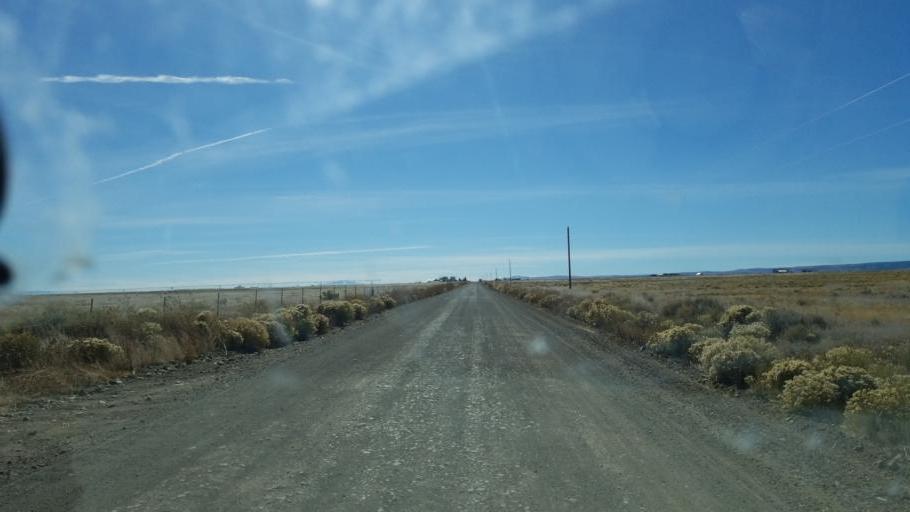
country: US
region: Colorado
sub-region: Rio Grande County
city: Monte Vista
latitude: 37.3948
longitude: -106.1496
